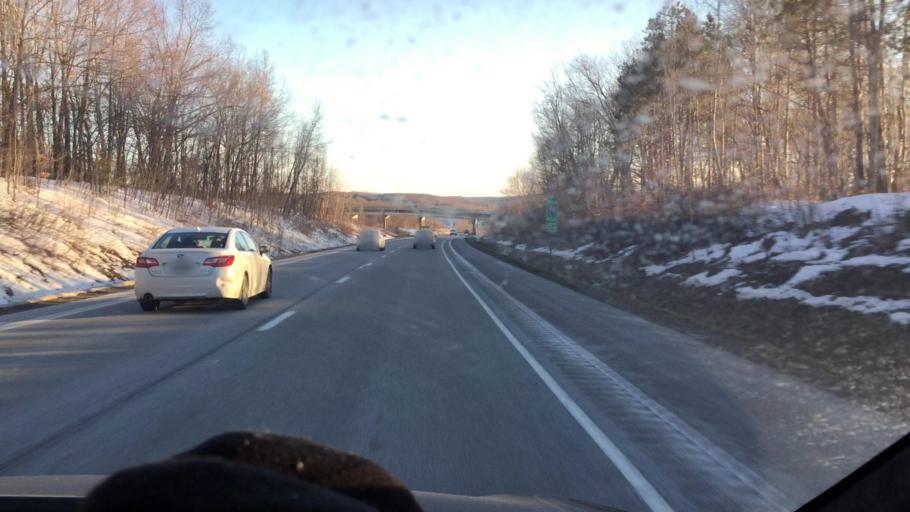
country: US
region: Pennsylvania
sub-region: Crawford County
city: Meadville
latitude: 41.7024
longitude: -80.2000
